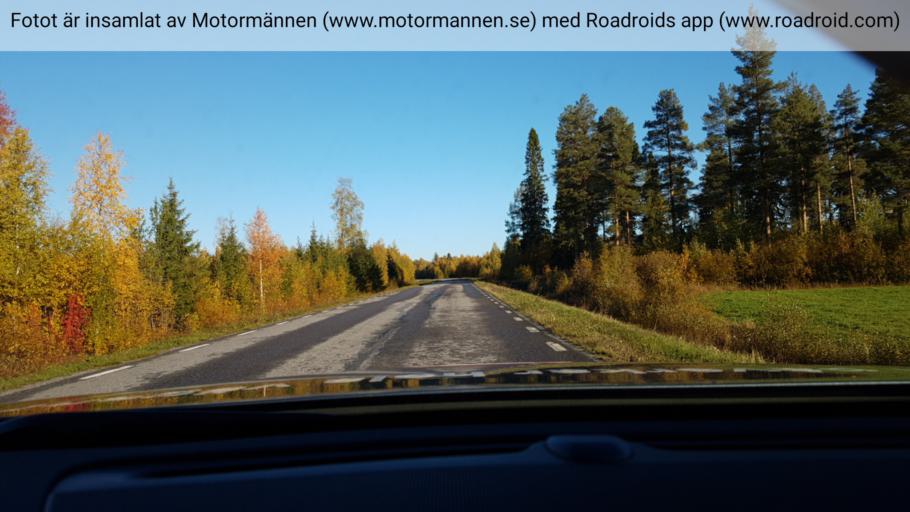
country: SE
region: Norrbotten
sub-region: Bodens Kommun
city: Boden
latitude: 65.9037
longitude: 21.6684
